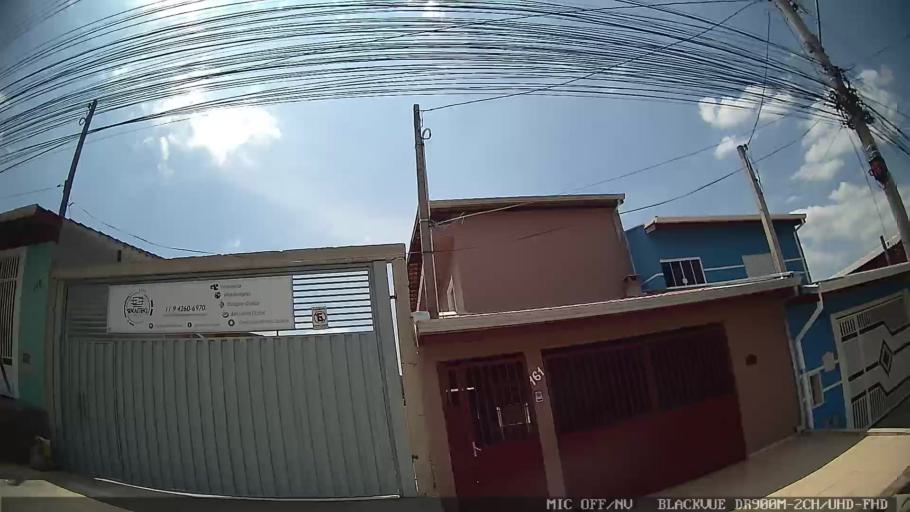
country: BR
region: Sao Paulo
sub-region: Cabreuva
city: Cabreuva
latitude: -23.2607
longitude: -47.0501
